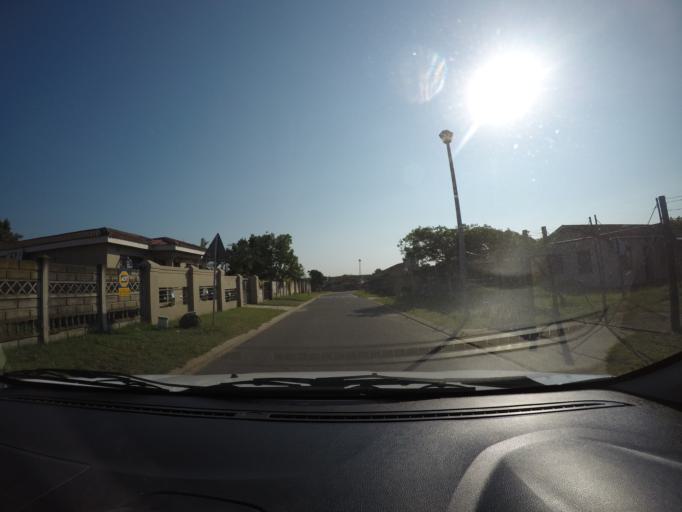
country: ZA
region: KwaZulu-Natal
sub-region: uThungulu District Municipality
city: Richards Bay
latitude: -28.7159
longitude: 32.0381
